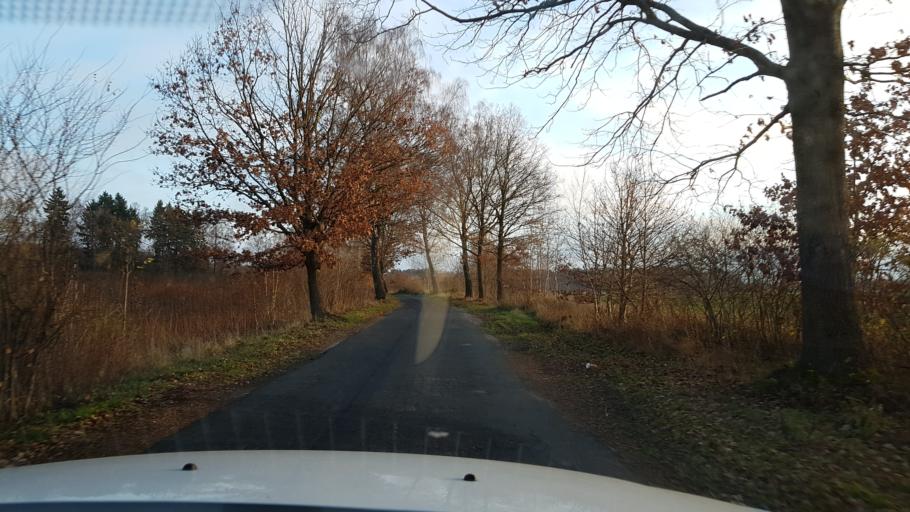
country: PL
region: West Pomeranian Voivodeship
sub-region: Koszalin
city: Koszalin
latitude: 54.1072
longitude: 16.1260
